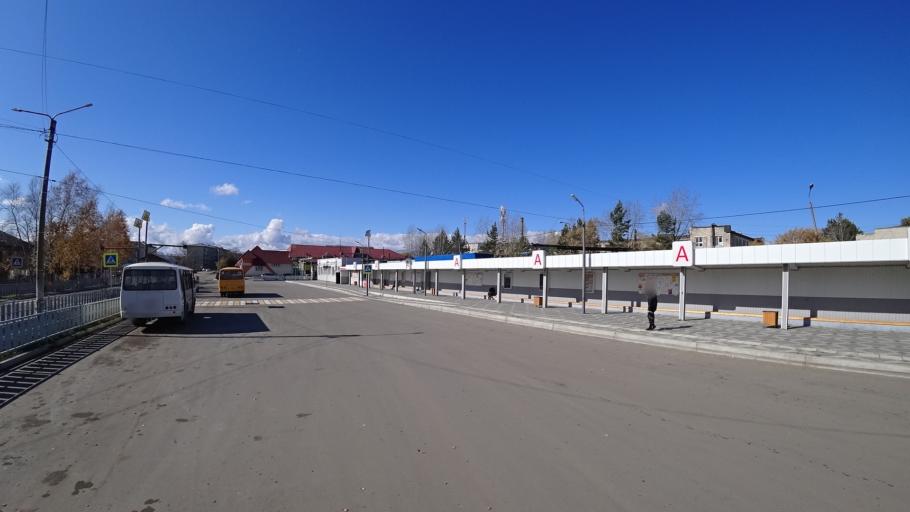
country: RU
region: Khabarovsk Krai
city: Amursk
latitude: 50.2186
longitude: 136.9009
